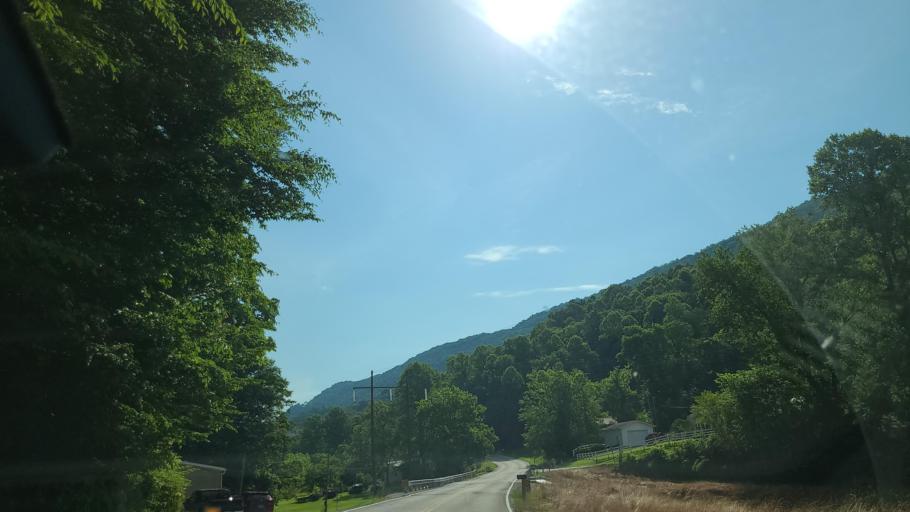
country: US
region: Kentucky
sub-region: Bell County
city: Pineville
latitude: 36.7094
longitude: -83.8288
